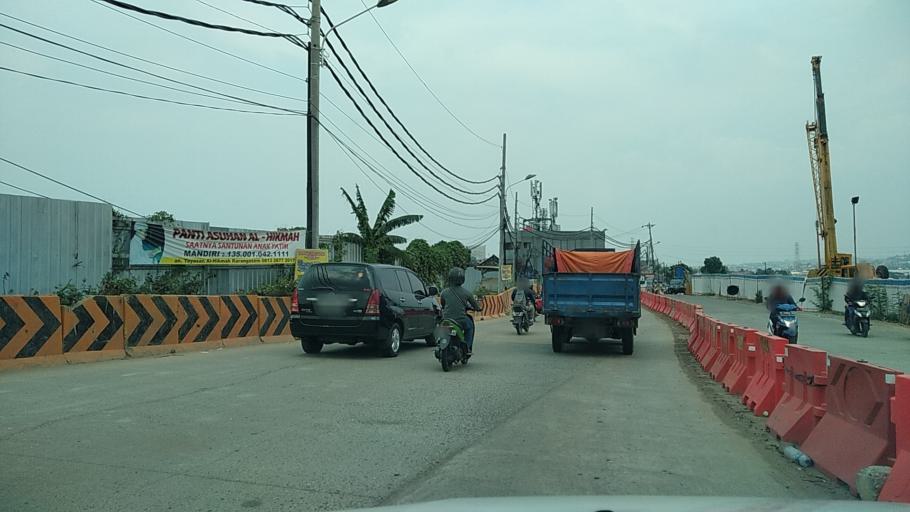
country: ID
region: Central Java
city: Semarang
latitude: -6.9944
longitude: 110.3488
